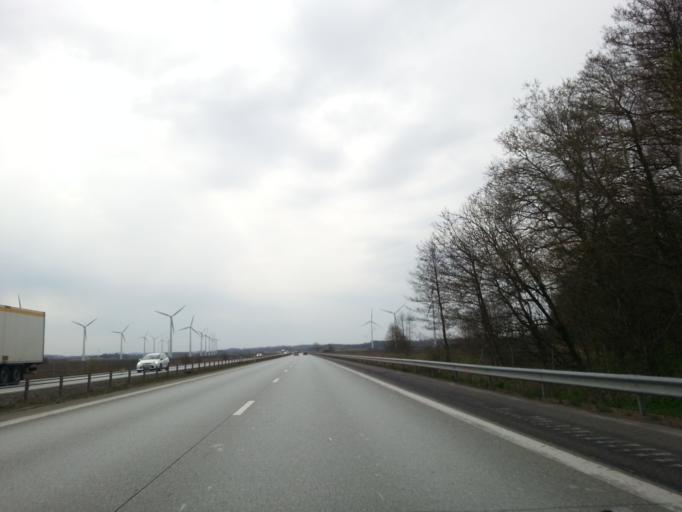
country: SE
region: Halland
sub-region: Falkenbergs Kommun
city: Falkenberg
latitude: 56.9556
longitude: 12.4609
